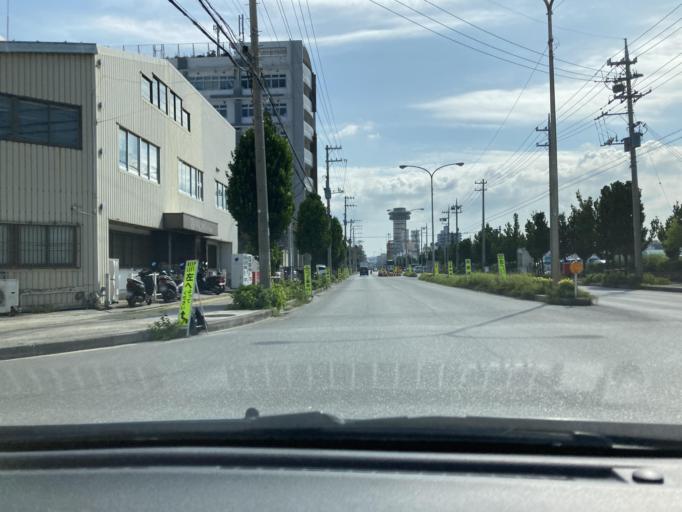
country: JP
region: Okinawa
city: Naha-shi
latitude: 26.2413
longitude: 127.6755
